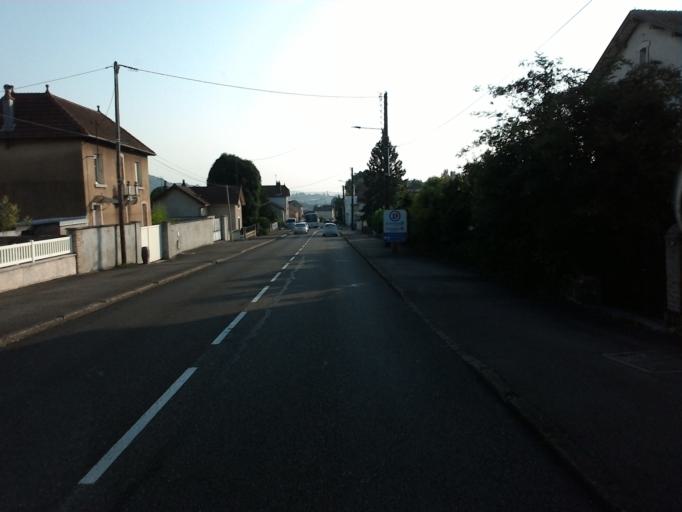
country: FR
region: Franche-Comte
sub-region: Departement de la Haute-Saone
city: Echenoz-la-Meline
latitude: 47.6099
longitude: 6.1460
